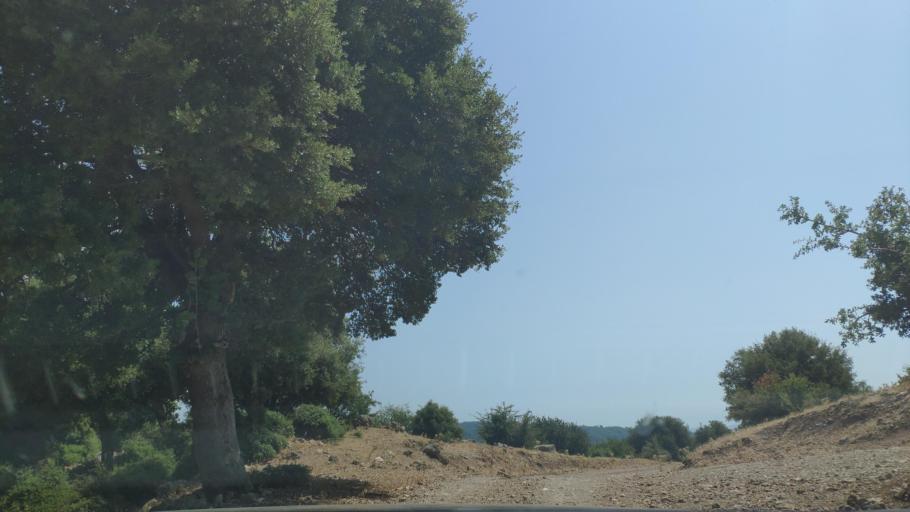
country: GR
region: West Greece
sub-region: Nomos Aitolias kai Akarnanias
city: Monastirakion
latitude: 38.8165
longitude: 21.0234
